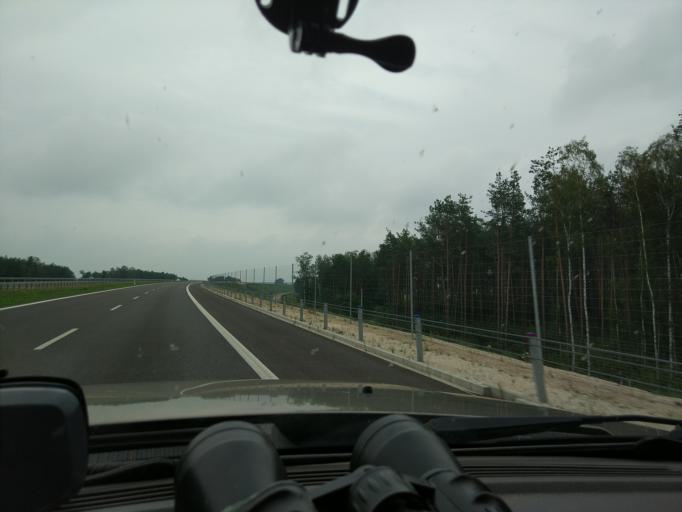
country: PL
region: Podlasie
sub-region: Powiat zambrowski
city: Szumowo
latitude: 52.9400
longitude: 22.1469
